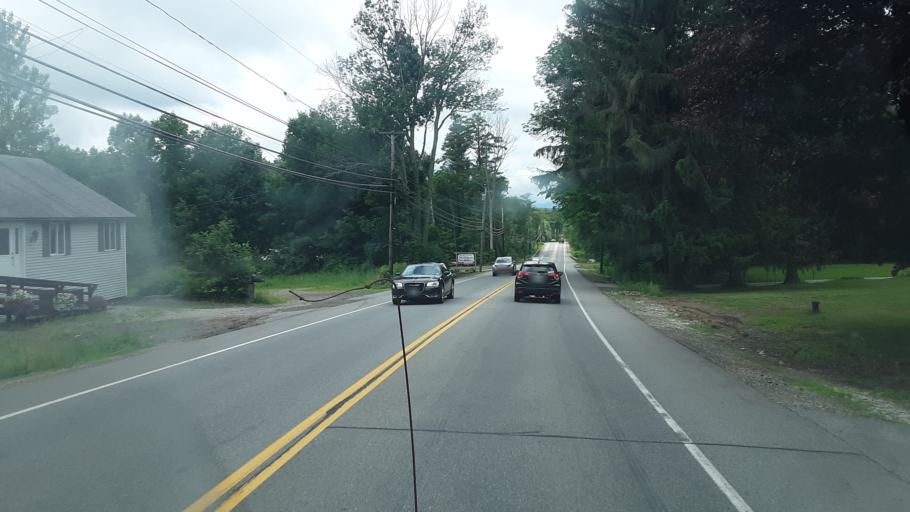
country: US
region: New Hampshire
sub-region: Rockingham County
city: Northwood
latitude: 43.2117
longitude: -71.1934
